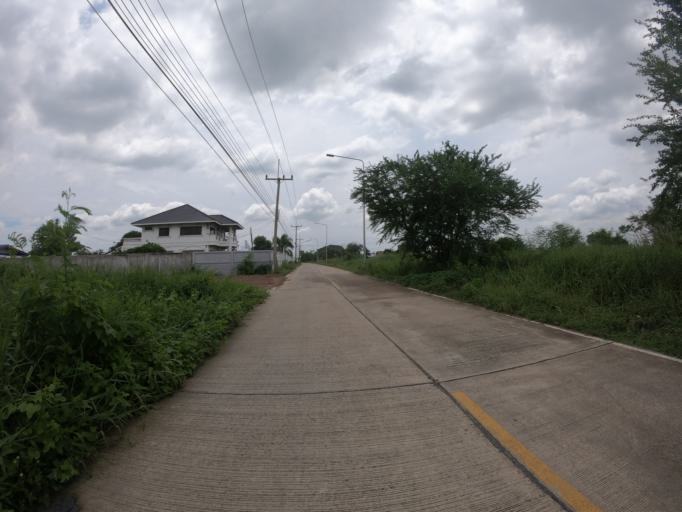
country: TH
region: Pathum Thani
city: Ban Lam Luk Ka
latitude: 13.9619
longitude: 100.8539
